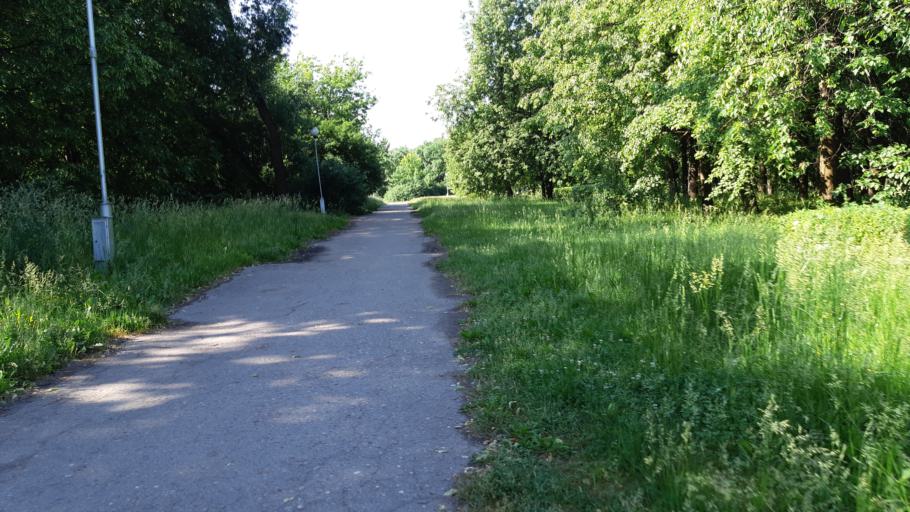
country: LT
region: Kauno apskritis
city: Dainava (Kaunas)
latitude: 54.9236
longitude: 23.9817
